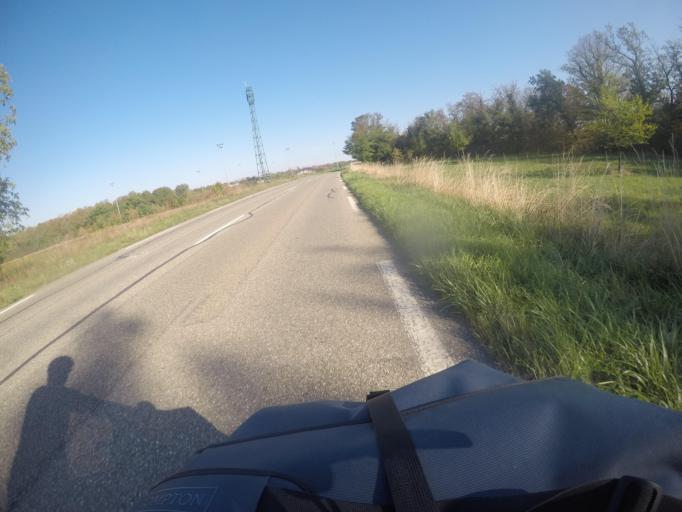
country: FR
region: Alsace
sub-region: Departement du Haut-Rhin
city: Kembs
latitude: 47.6661
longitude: 7.4988
